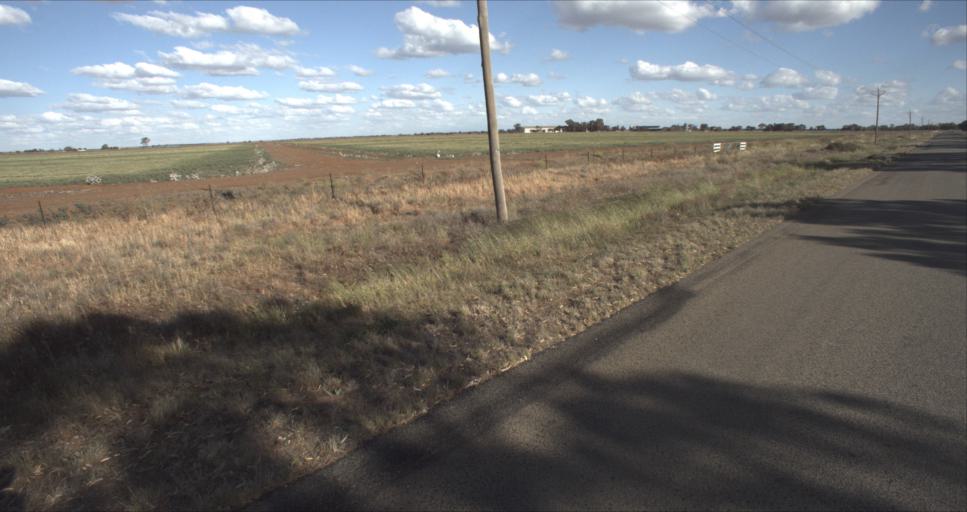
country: AU
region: New South Wales
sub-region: Leeton
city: Leeton
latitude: -34.5448
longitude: 146.2796
